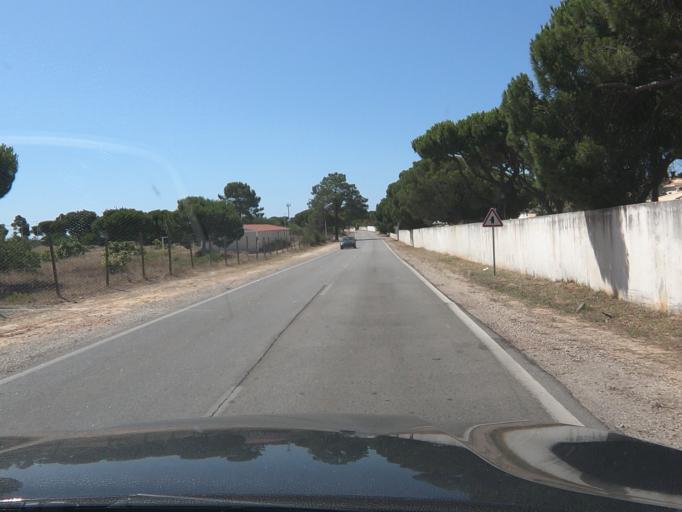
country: PT
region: Faro
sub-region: Loule
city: Vilamoura
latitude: 37.0862
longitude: -8.1011
